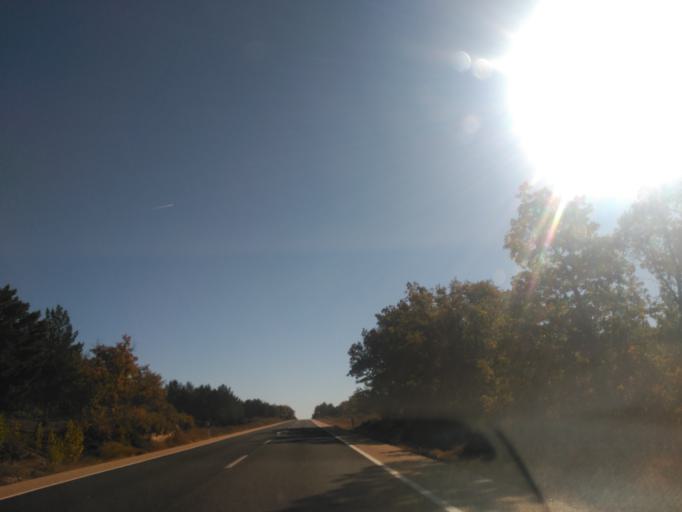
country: ES
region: Castille and Leon
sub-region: Provincia de Soria
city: Cidones
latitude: 41.8109
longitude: -2.6983
